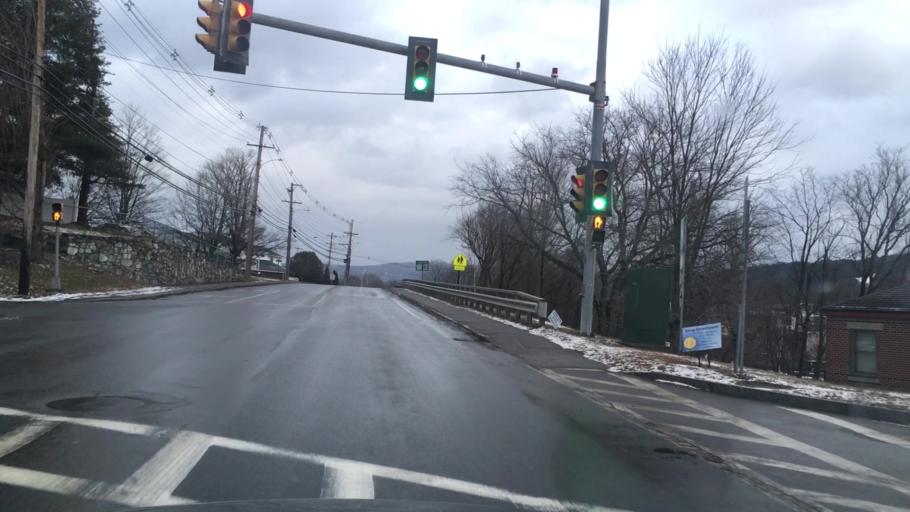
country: US
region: New Hampshire
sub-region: Sullivan County
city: Claremont
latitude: 43.3758
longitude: -72.3384
